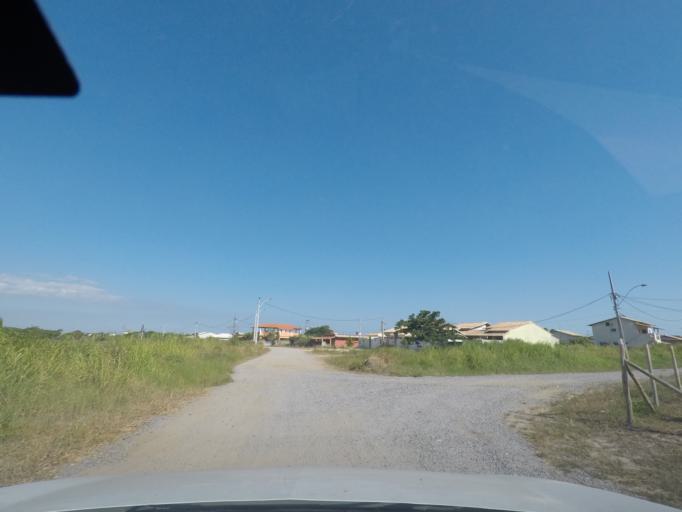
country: BR
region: Rio de Janeiro
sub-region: Marica
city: Marica
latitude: -22.9655
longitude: -42.9191
